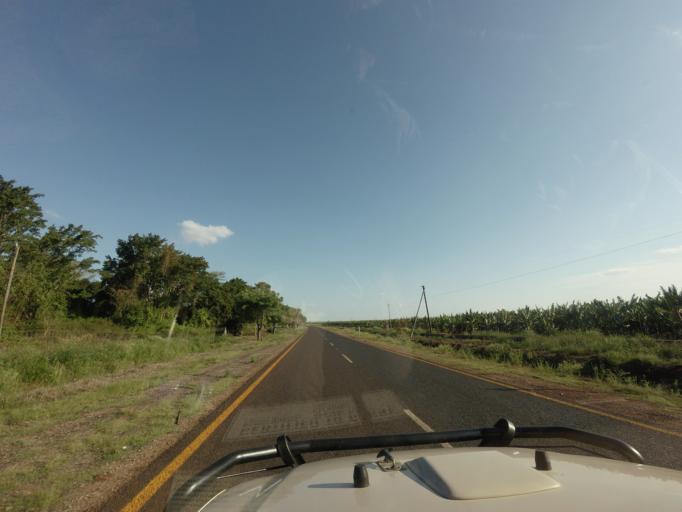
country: ZA
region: Mpumalanga
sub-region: Ehlanzeni District
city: Komatipoort
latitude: -25.3861
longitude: 31.9116
